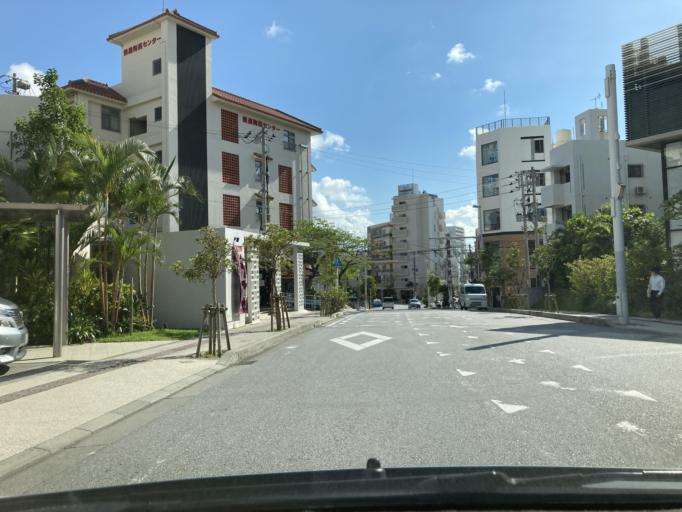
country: JP
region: Okinawa
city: Naha-shi
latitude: 26.2144
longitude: 127.6904
